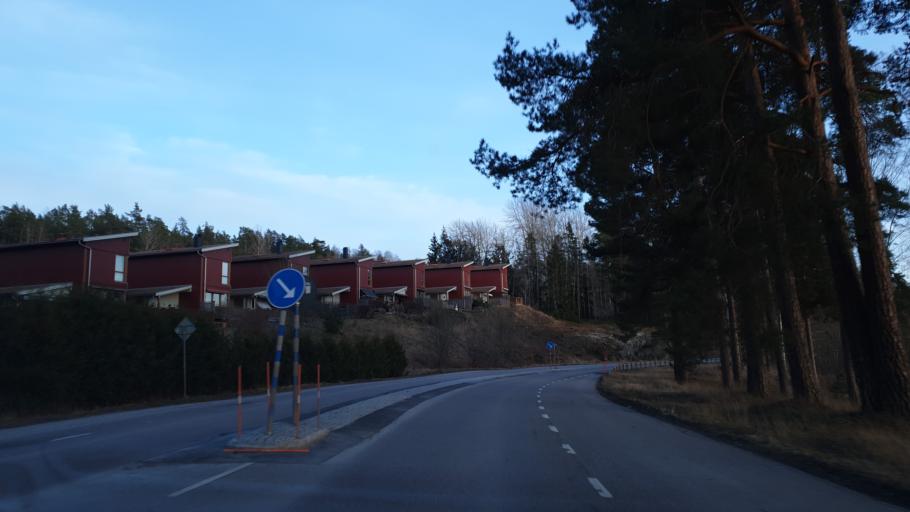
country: SE
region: Uppsala
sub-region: Habo Kommun
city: Balsta
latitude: 59.5504
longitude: 17.5580
